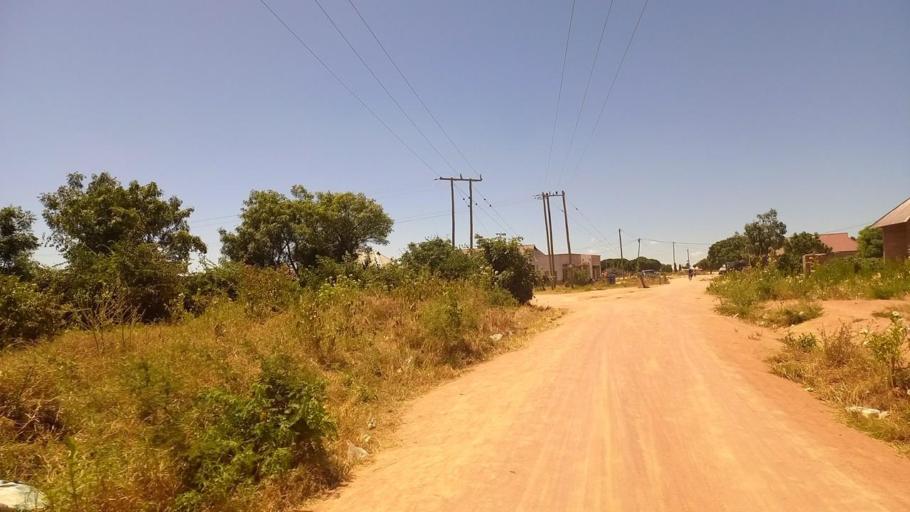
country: TZ
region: Dodoma
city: Dodoma
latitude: -6.1298
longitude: 35.7284
